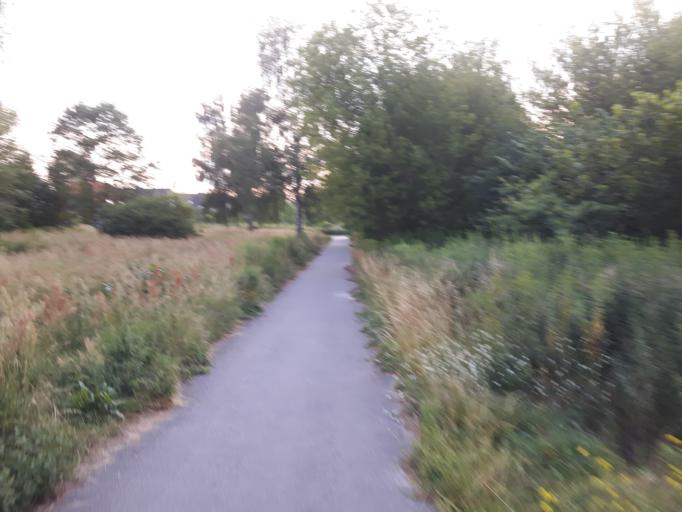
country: DE
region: Berlin
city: Staaken
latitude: 52.5525
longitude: 13.1397
